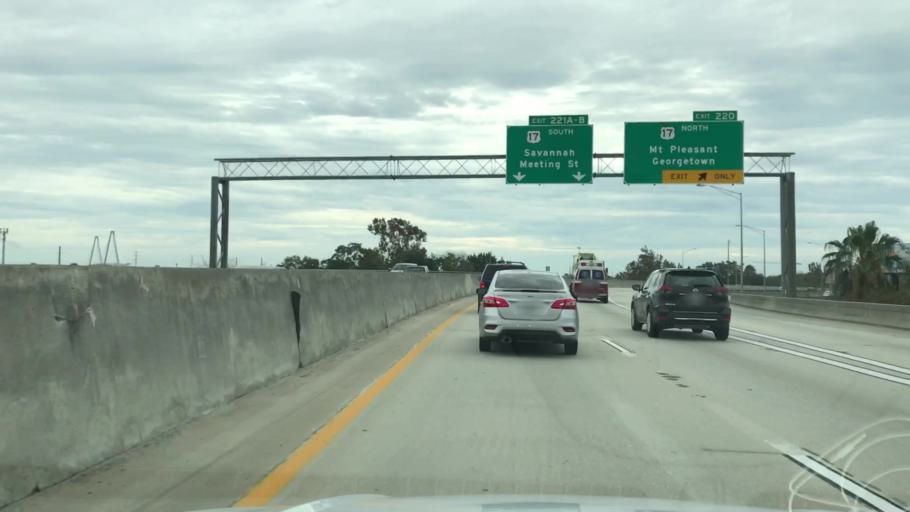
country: US
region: South Carolina
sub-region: Charleston County
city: Charleston
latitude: 32.8111
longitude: -79.9511
